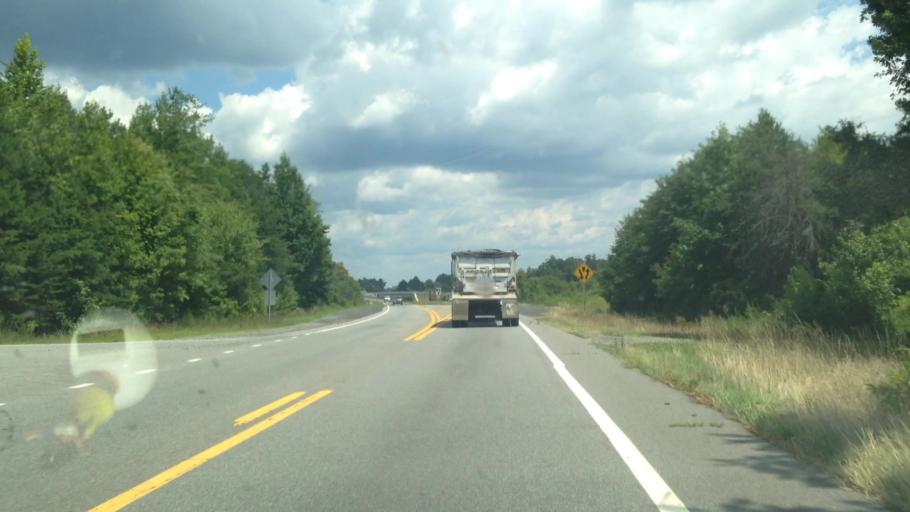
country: US
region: North Carolina
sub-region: Guilford County
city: Stokesdale
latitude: 36.2785
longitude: -79.9416
